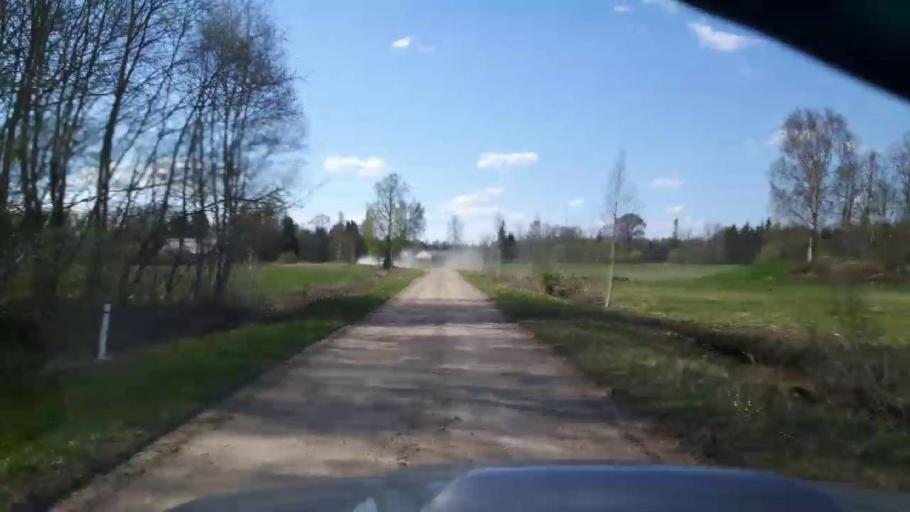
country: EE
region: Paernumaa
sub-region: Tootsi vald
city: Tootsi
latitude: 58.4483
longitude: 24.8633
